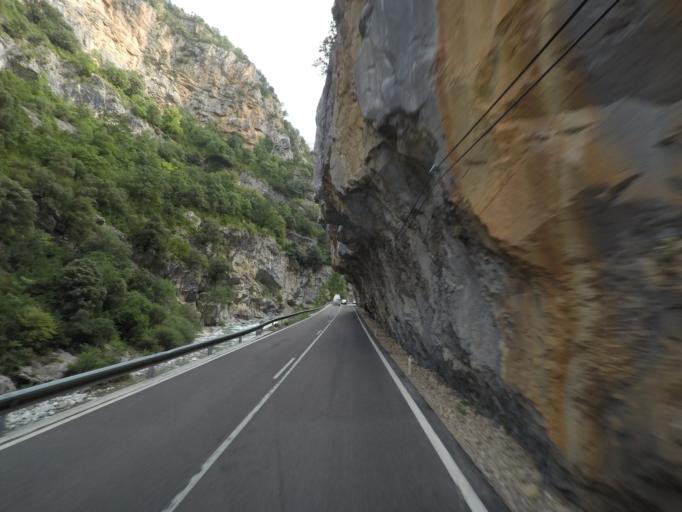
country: ES
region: Aragon
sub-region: Provincia de Huesca
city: Bielsa
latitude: 42.5632
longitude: 0.2043
